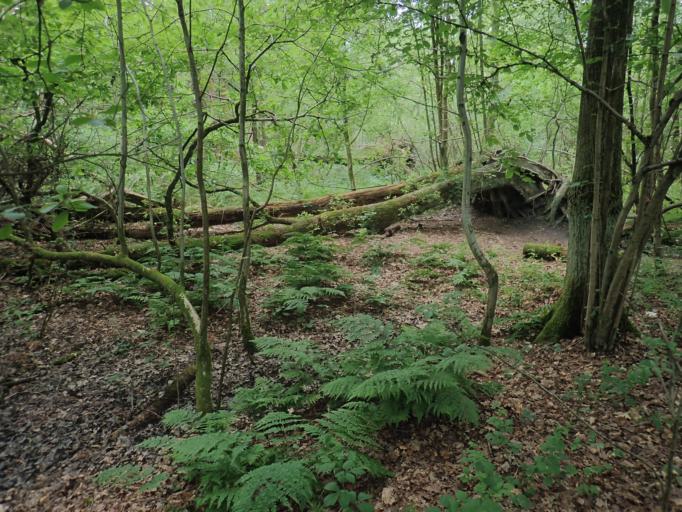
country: BE
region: Flanders
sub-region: Provincie Antwerpen
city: Zandhoven
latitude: 51.2477
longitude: 4.6747
